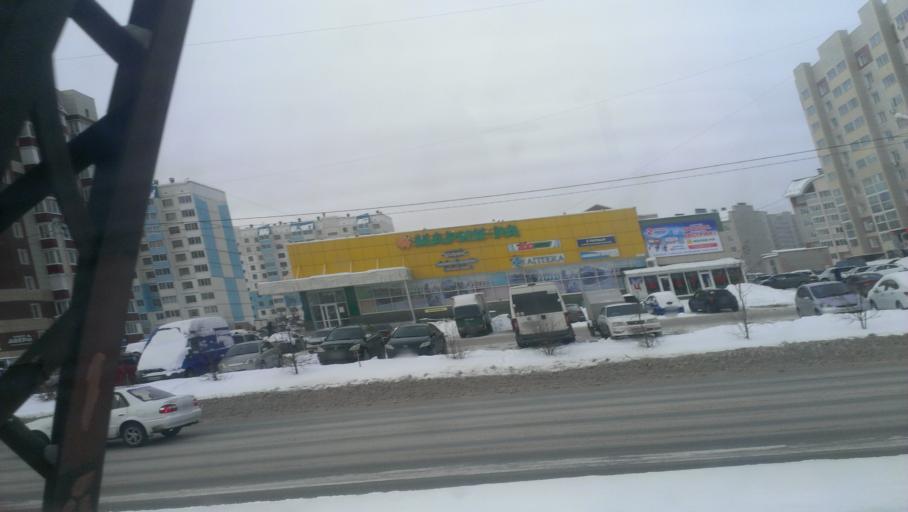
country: RU
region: Altai Krai
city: Novosilikatnyy
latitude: 53.3315
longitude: 83.6931
